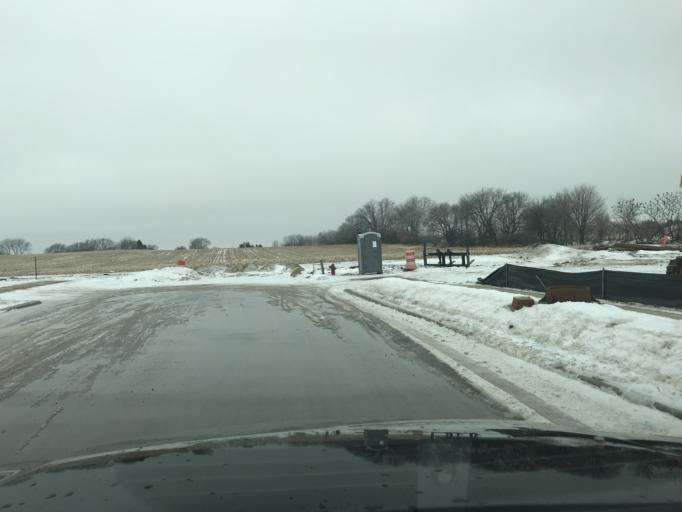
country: US
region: Wisconsin
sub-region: Dane County
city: Cottage Grove
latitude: 43.0965
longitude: -89.2242
